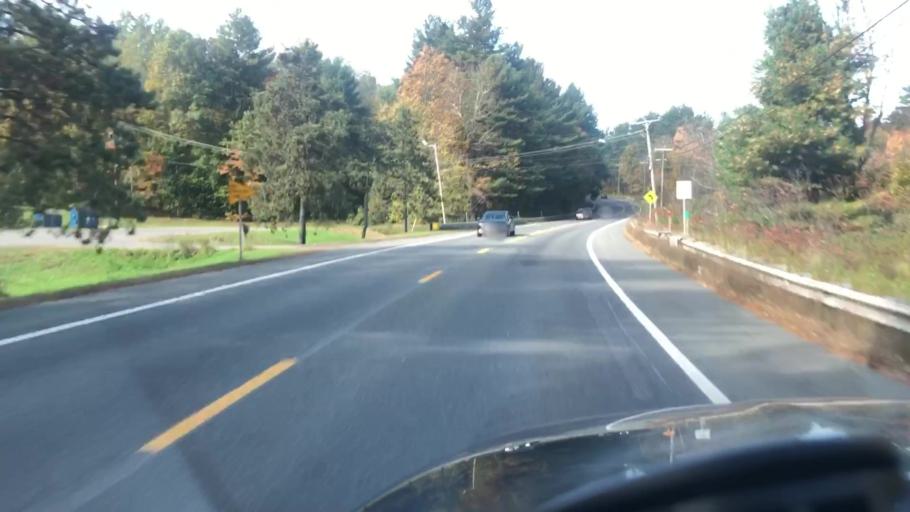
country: US
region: Massachusetts
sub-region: Franklin County
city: Shelburne
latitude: 42.6108
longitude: -72.6595
